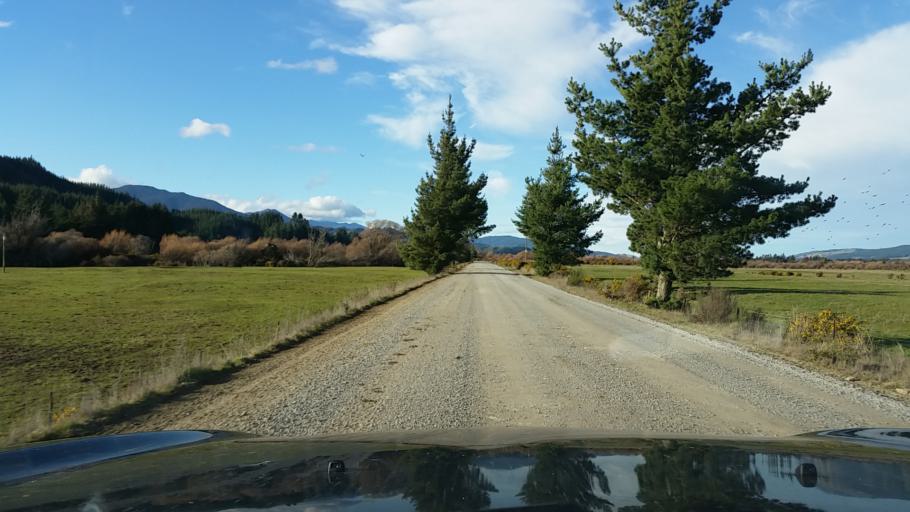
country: NZ
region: Nelson
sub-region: Nelson City
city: Nelson
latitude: -41.5690
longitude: 173.4537
